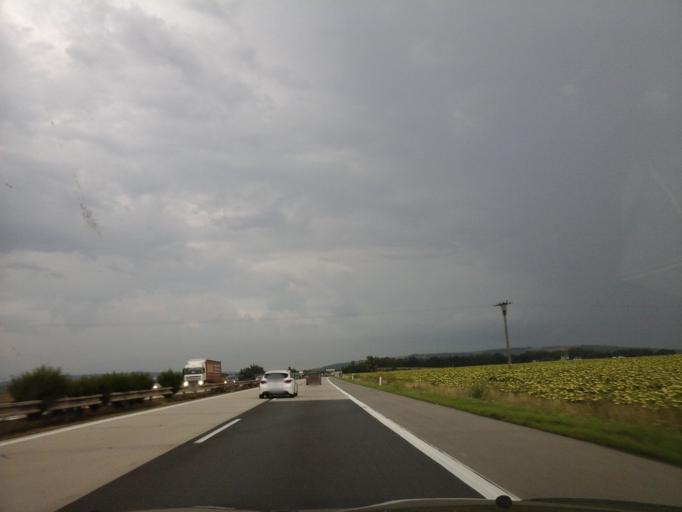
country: CZ
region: South Moravian
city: Rajhradice
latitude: 49.1032
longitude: 16.6535
